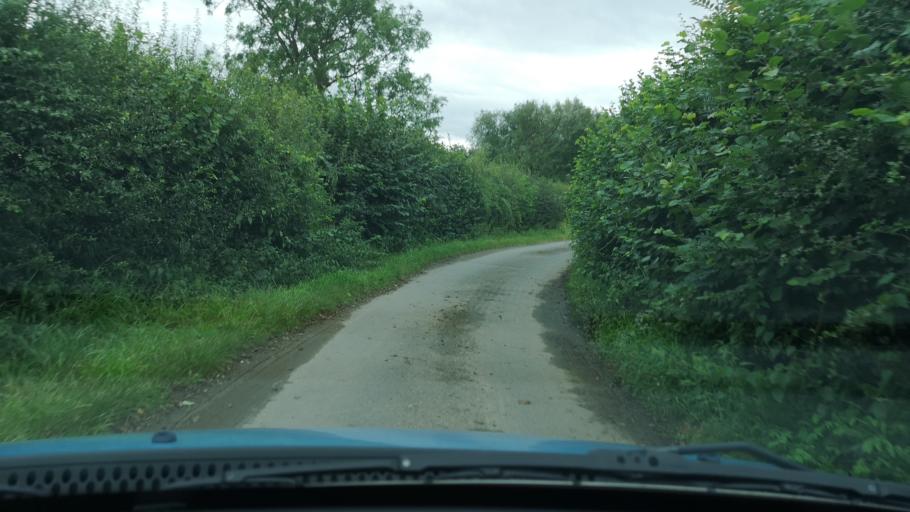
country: GB
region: England
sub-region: City and Borough of Wakefield
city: Featherstone
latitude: 53.6557
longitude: -1.3497
